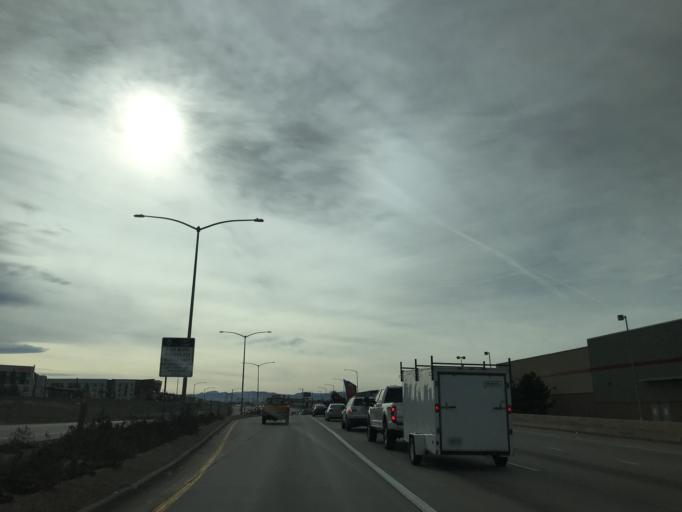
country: US
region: Colorado
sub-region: Arapahoe County
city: Englewood
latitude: 39.6447
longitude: -105.0050
